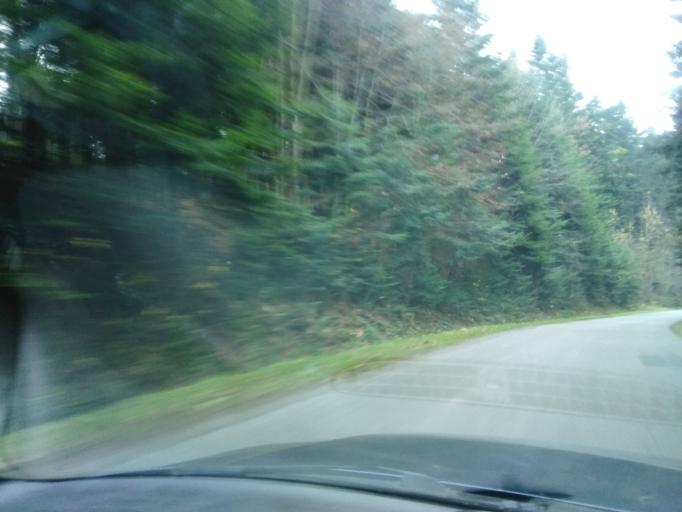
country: PL
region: Subcarpathian Voivodeship
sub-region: Powiat strzyzowski
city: Wysoka Strzyzowska
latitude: 49.8293
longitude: 21.7754
